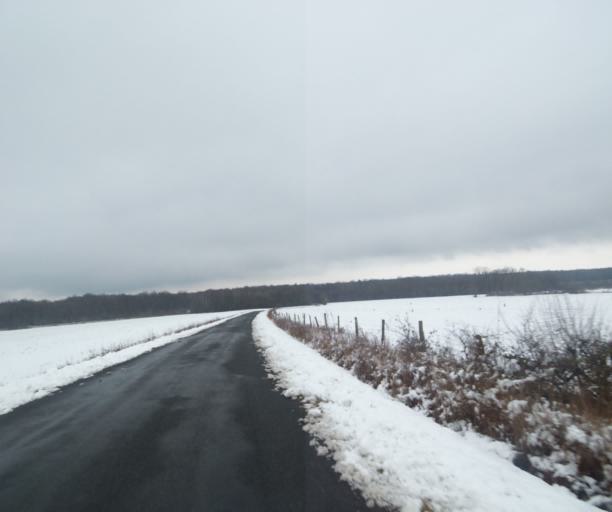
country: FR
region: Champagne-Ardenne
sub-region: Departement de la Haute-Marne
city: Laneuville-a-Remy
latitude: 48.4918
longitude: 4.8680
